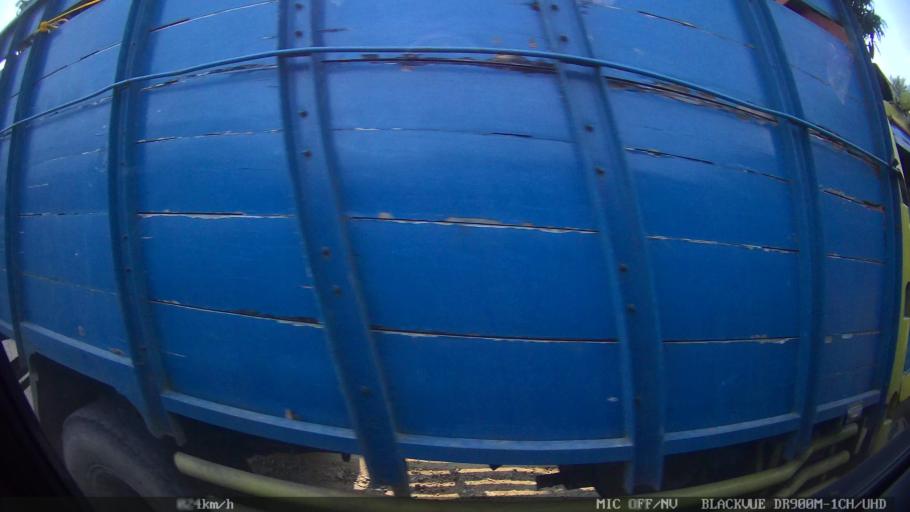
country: ID
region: Lampung
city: Pringsewu
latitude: -5.3936
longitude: 104.9926
